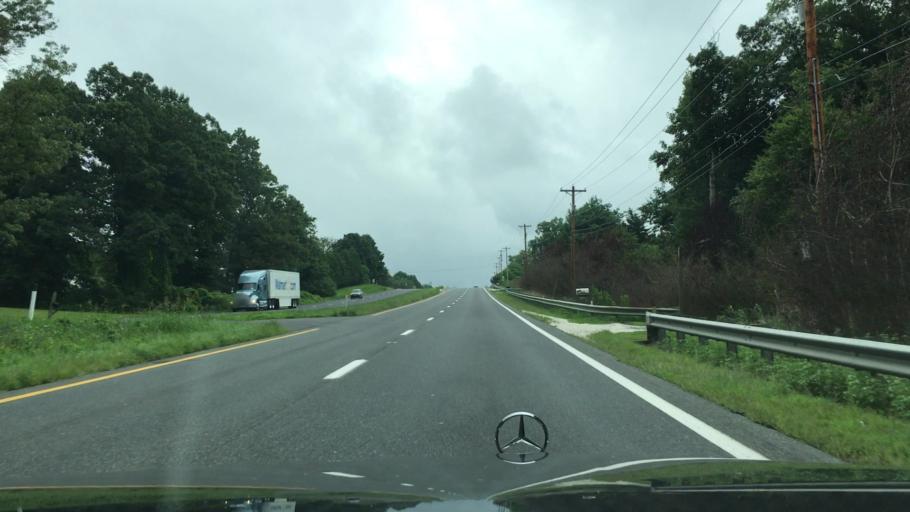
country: US
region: Virginia
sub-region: Campbell County
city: Concord
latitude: 37.3670
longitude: -79.0128
